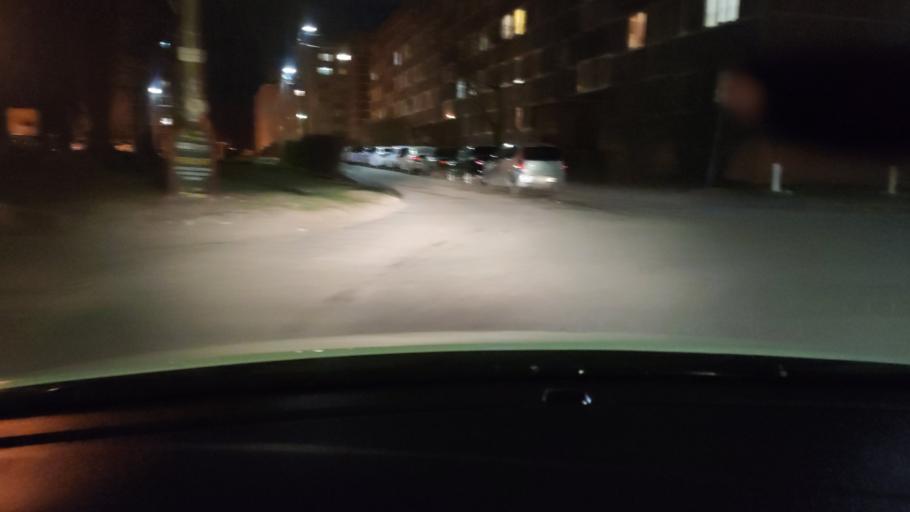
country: RU
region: Voronezj
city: Semiluki
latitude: 51.6966
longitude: 39.0126
